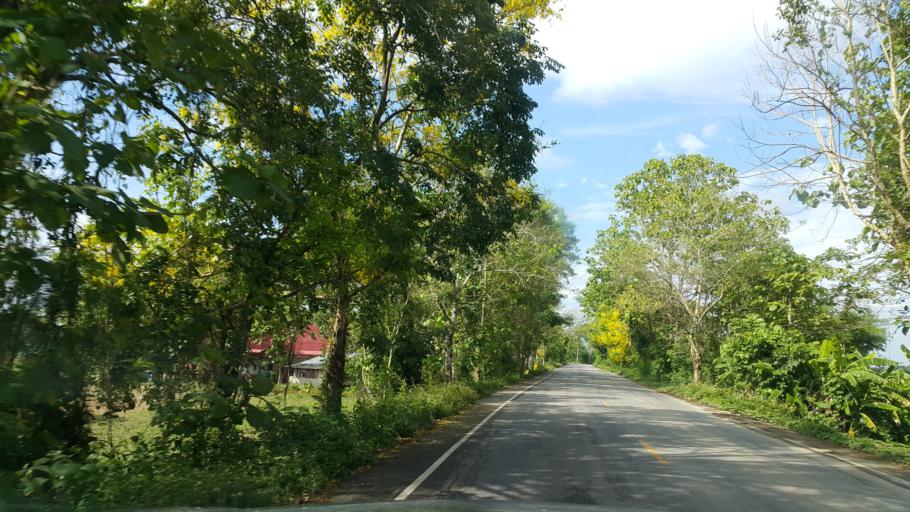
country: TH
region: Chiang Rai
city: Wiang Chai
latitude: 19.9311
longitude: 99.9074
